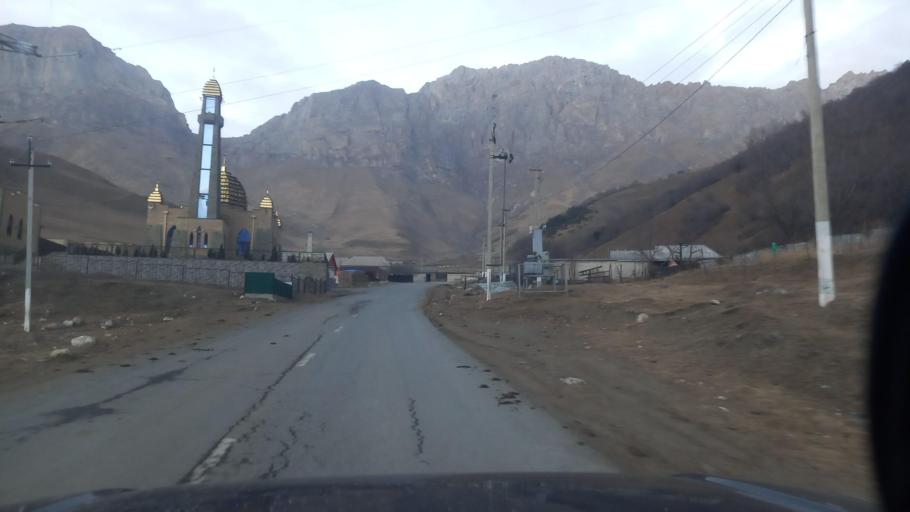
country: RU
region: Ingushetiya
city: Dzhayrakh
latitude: 42.8146
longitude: 44.8132
